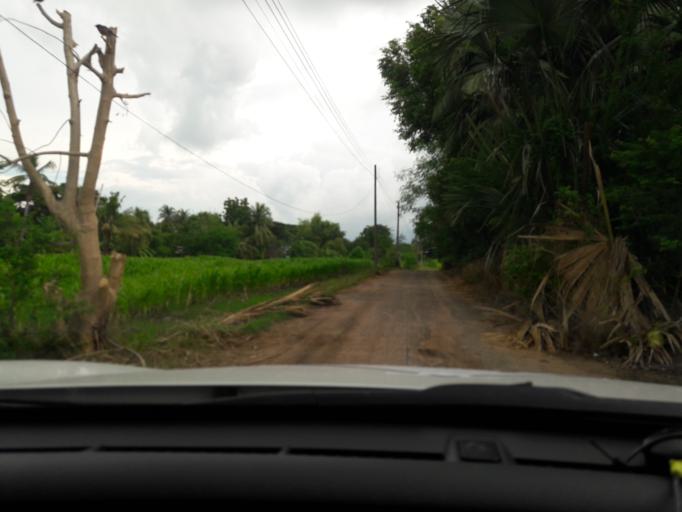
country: TH
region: Nakhon Sawan
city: Tak Fa
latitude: 15.3570
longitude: 100.4950
